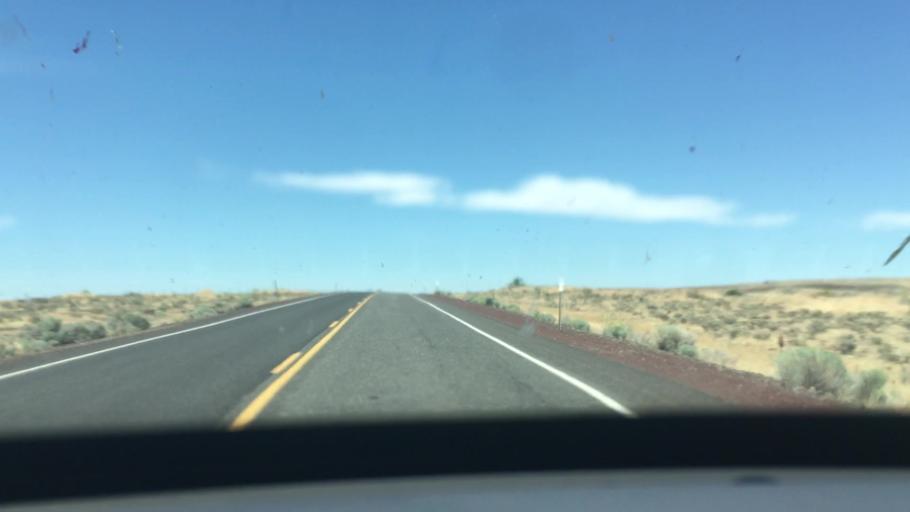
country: US
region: Oregon
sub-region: Jefferson County
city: Madras
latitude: 44.9862
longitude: -120.8613
